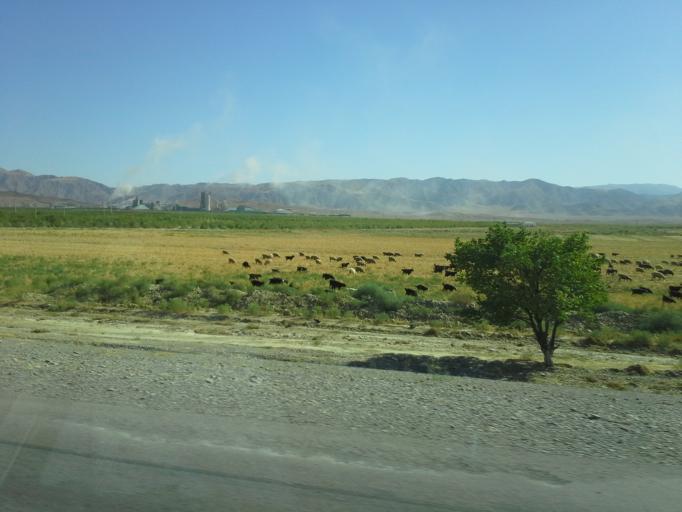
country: TM
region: Ahal
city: Baharly
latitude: 38.2870
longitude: 57.6567
